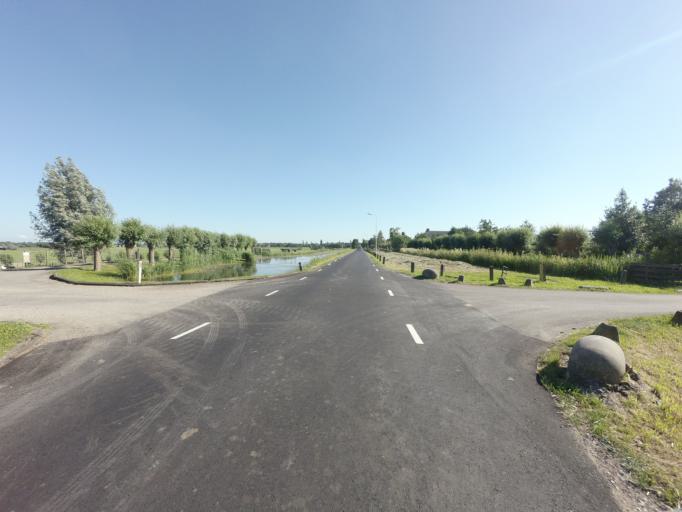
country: NL
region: South Holland
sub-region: Gemeente Waddinxveen
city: Oranjewijk
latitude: 52.0519
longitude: 4.6798
